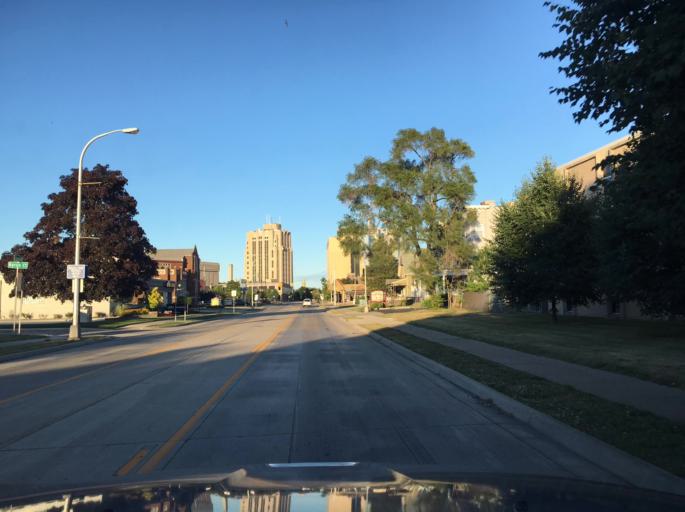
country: US
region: Michigan
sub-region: Macomb County
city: Mount Clemens
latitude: 42.5973
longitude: -82.8827
